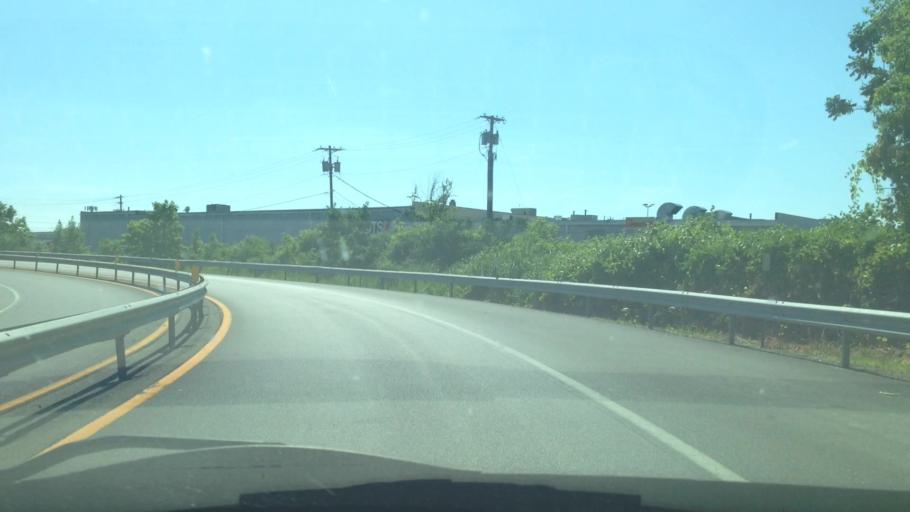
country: US
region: New York
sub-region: Oneida County
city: Utica
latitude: 43.1136
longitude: -75.2040
